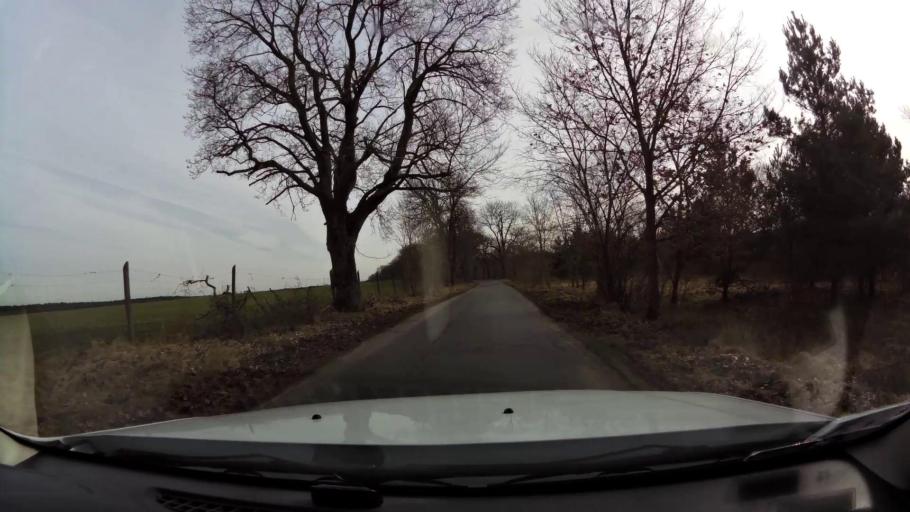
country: PL
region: West Pomeranian Voivodeship
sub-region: Powiat stargardzki
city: Insko
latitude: 53.4544
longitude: 15.6205
